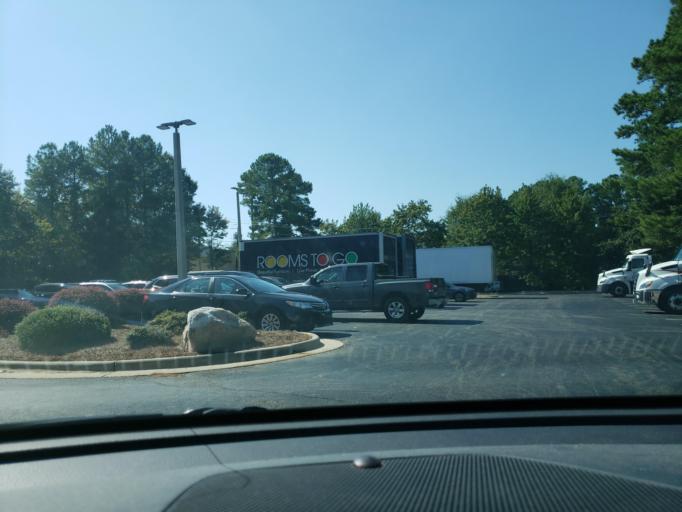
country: US
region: North Carolina
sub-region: Wake County
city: West Raleigh
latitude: 35.8547
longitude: -78.6985
